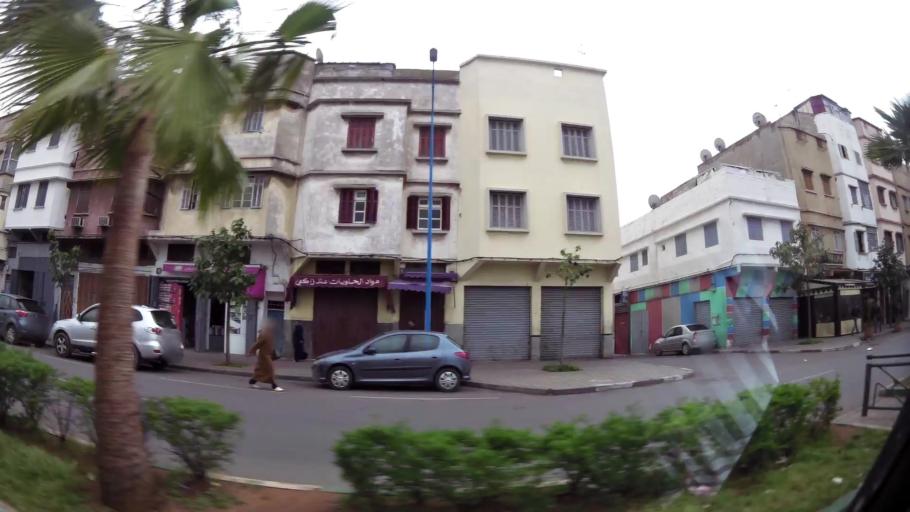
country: MA
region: Grand Casablanca
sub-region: Casablanca
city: Casablanca
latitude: 33.5833
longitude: -7.5588
